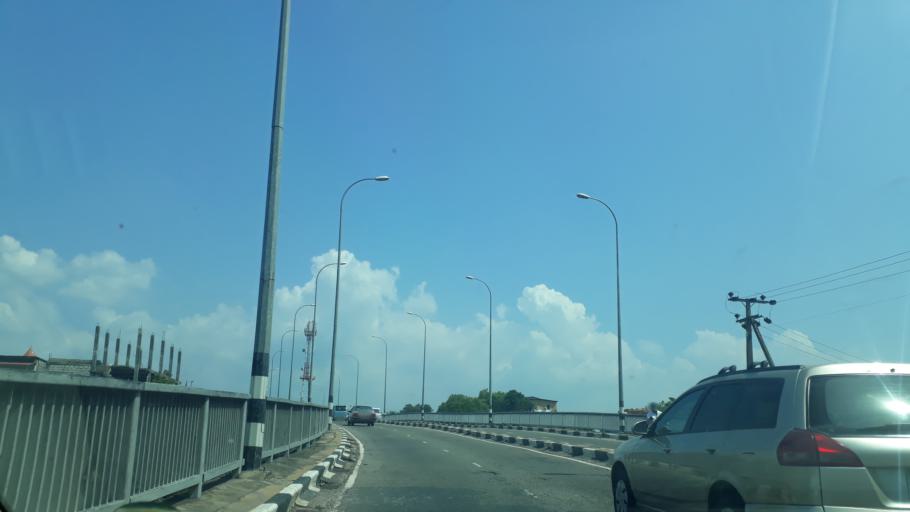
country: LK
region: Western
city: Gampaha
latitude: 7.0915
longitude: 79.9910
